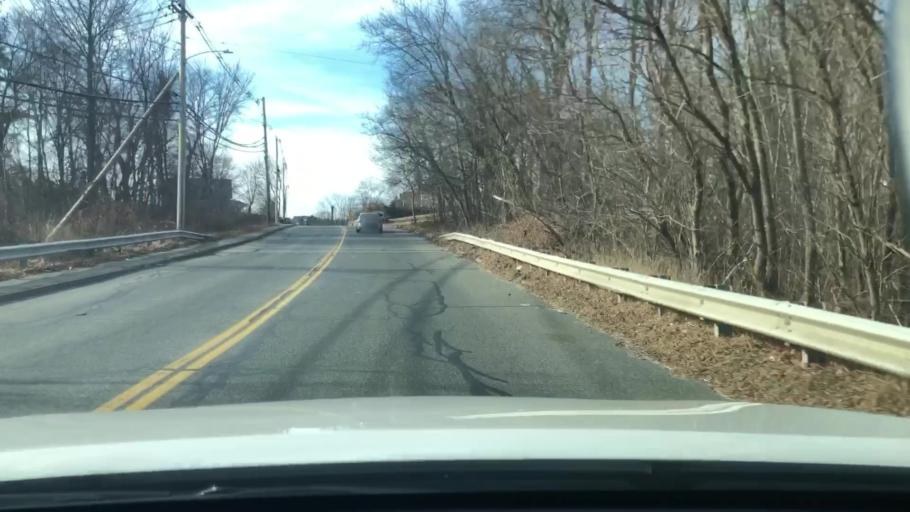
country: US
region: Massachusetts
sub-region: Worcester County
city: Millbury
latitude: 42.1927
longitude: -71.7440
